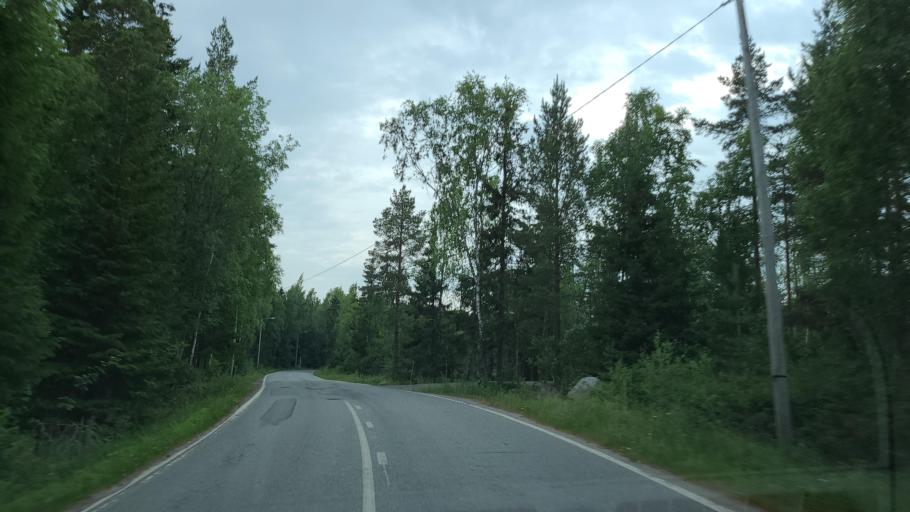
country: FI
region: Ostrobothnia
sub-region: Vaasa
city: Replot
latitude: 63.1744
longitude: 21.2774
